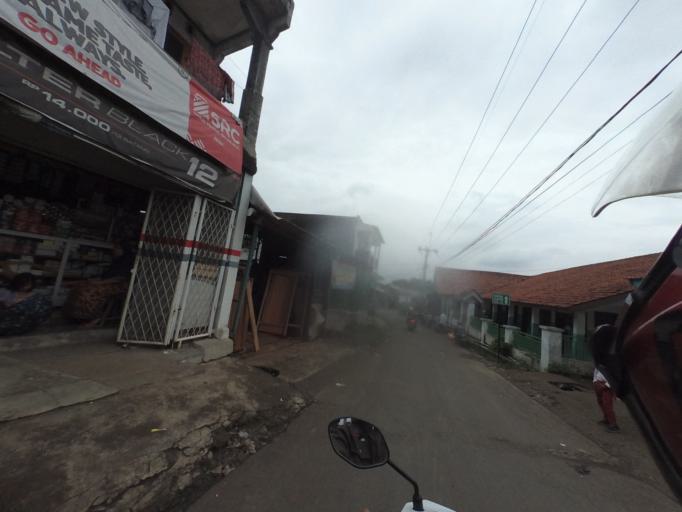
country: ID
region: West Java
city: Bogor
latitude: -6.6200
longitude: 106.7462
